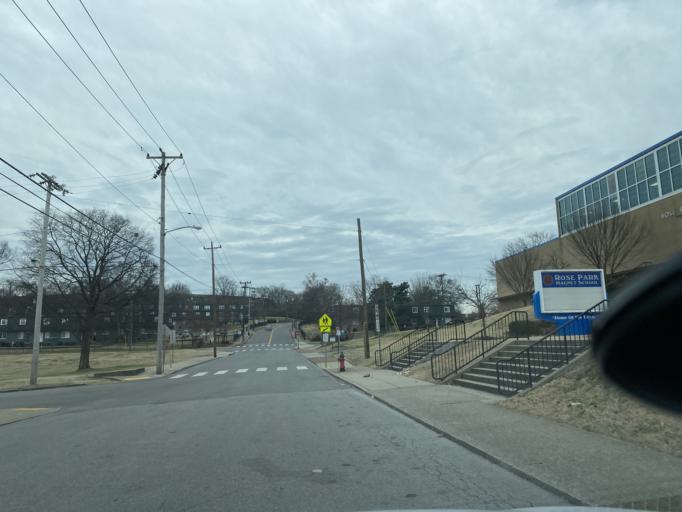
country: US
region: Tennessee
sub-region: Davidson County
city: Nashville
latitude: 36.1429
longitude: -86.7808
